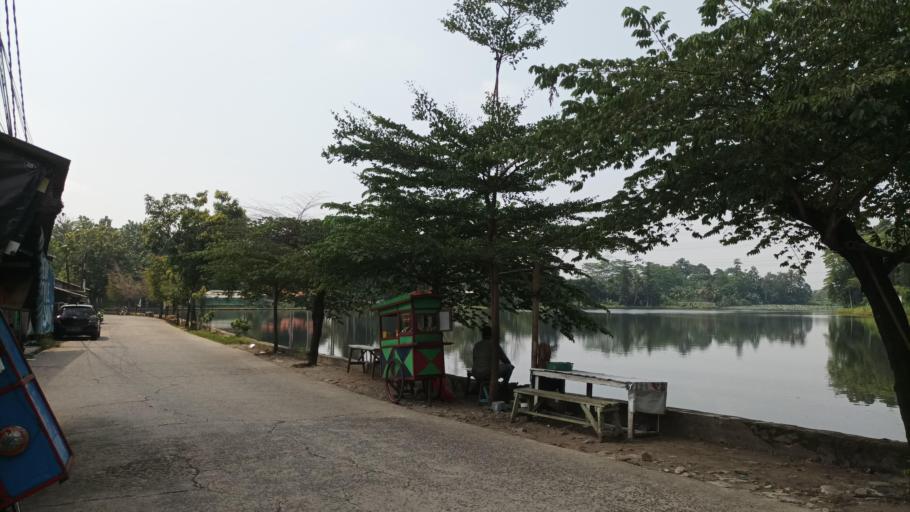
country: ID
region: West Java
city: Depok
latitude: -6.4204
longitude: 106.8595
